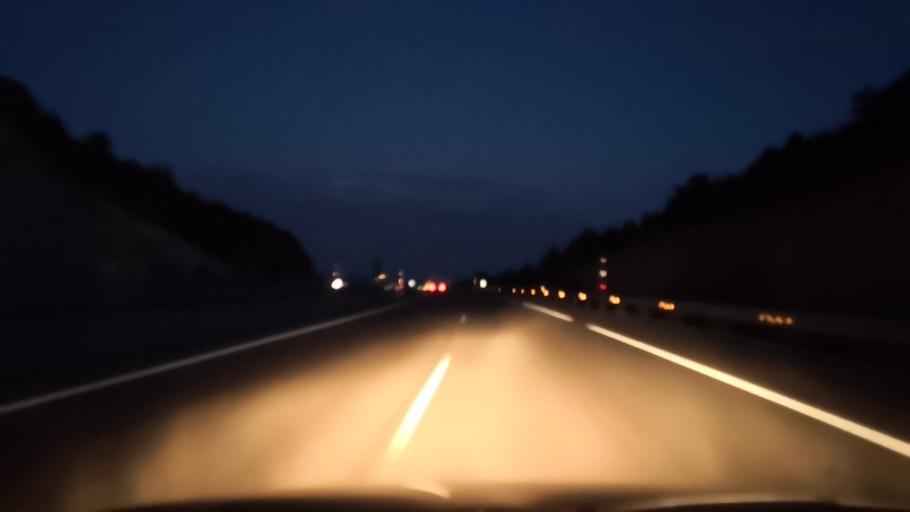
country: ES
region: Castille and Leon
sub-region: Provincia de Leon
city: Villagaton
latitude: 42.5655
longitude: -6.2115
